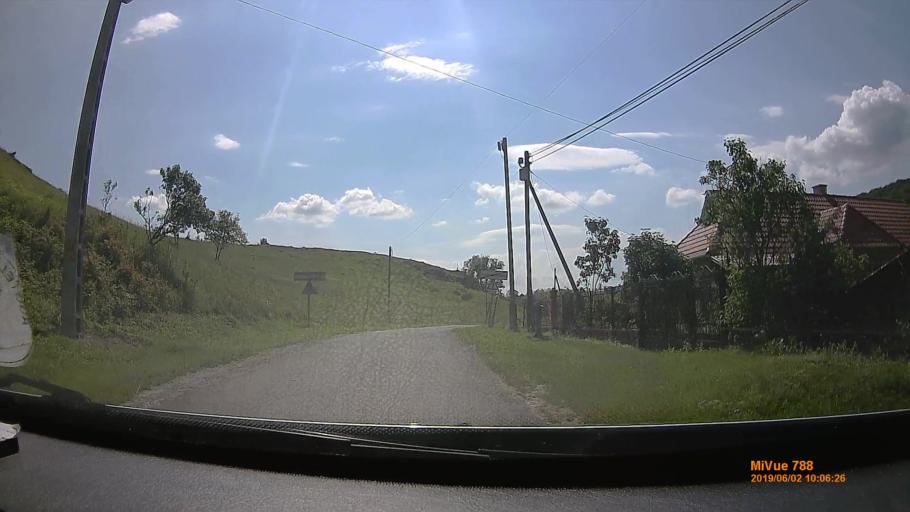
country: HU
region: Borsod-Abauj-Zemplen
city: Szendro
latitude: 48.5174
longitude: 20.7786
